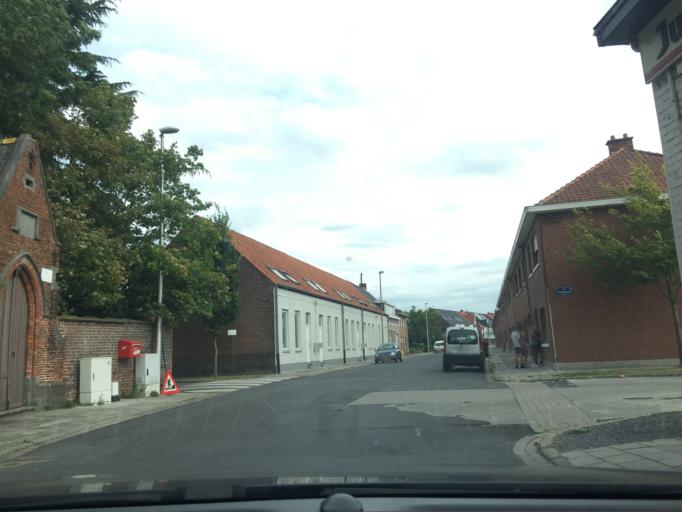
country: BE
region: Flanders
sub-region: Provincie West-Vlaanderen
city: Izegem
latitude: 50.9153
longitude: 3.2259
